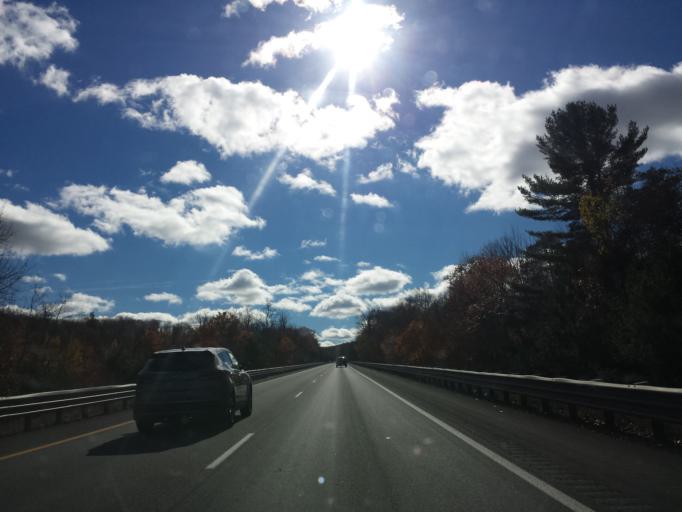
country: US
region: Michigan
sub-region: Cheboygan County
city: Indian River
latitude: 45.3667
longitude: -84.6109
